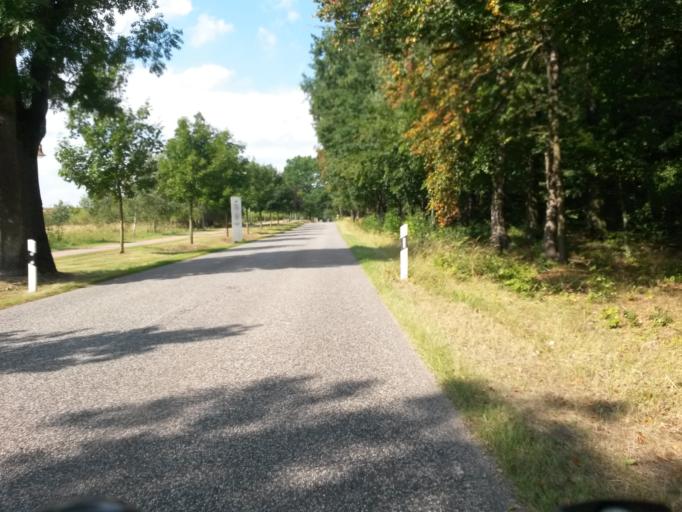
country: DE
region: Brandenburg
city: Templin
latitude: 53.1008
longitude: 13.5294
